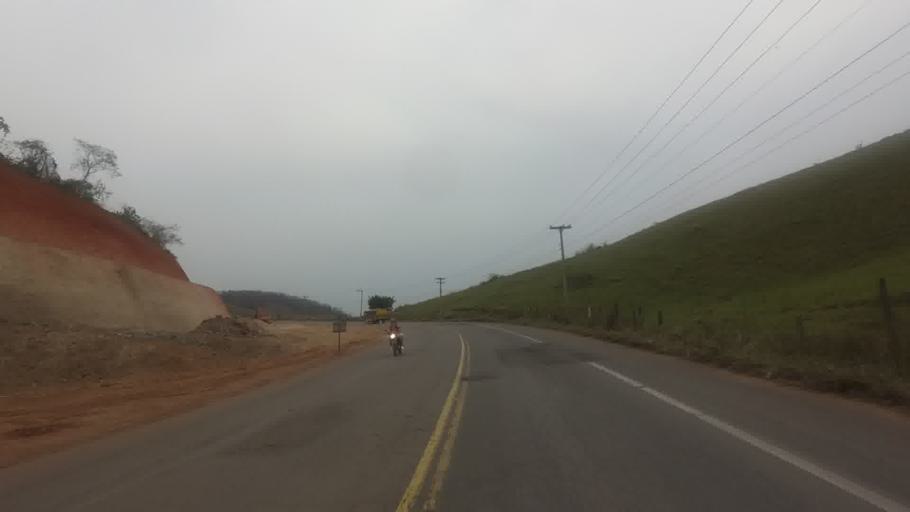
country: BR
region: Rio de Janeiro
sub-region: Santo Antonio De Padua
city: Santo Antonio de Padua
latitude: -21.6084
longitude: -42.2506
